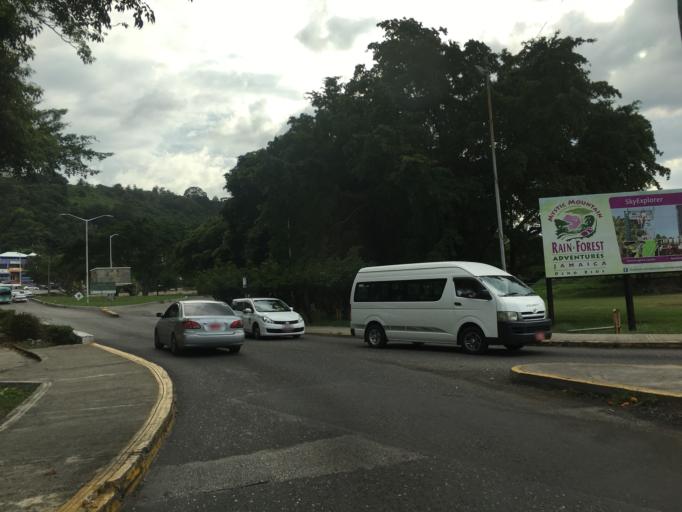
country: JM
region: Saint James
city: Montego Bay
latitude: 18.4962
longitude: -77.9169
